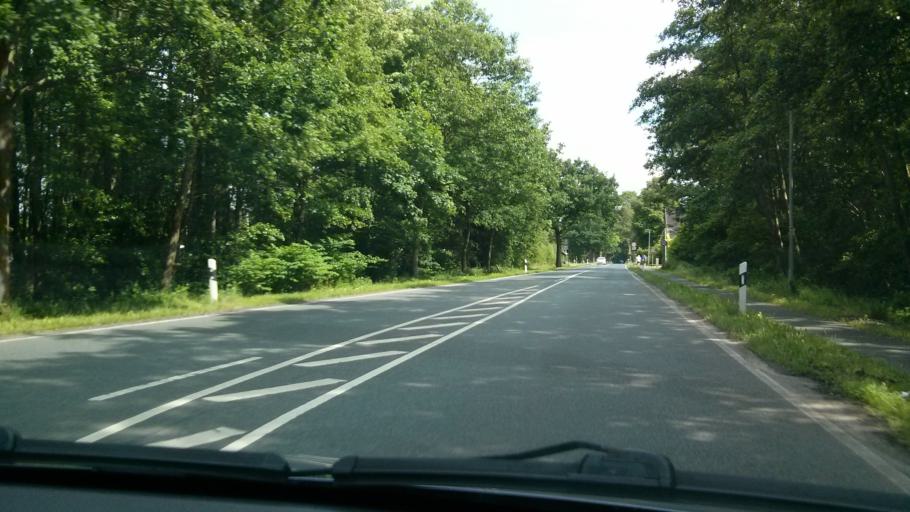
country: DE
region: Lower Saxony
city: Schiffdorf
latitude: 53.5240
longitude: 8.6651
